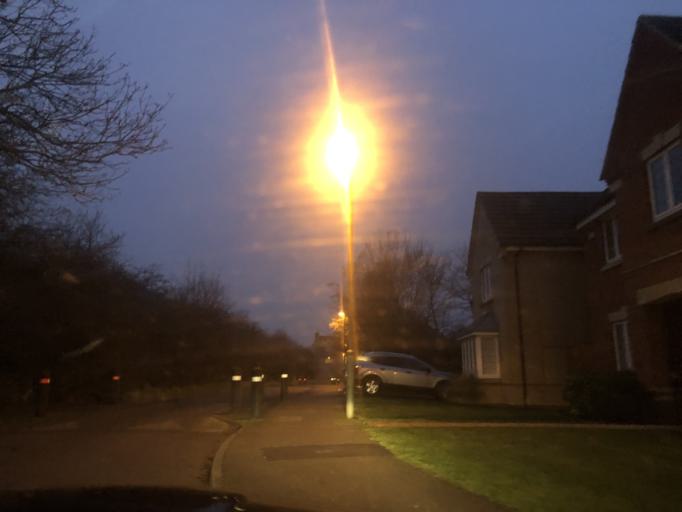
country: GB
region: England
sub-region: Oxfordshire
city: Bicester
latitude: 51.9092
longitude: -1.1648
